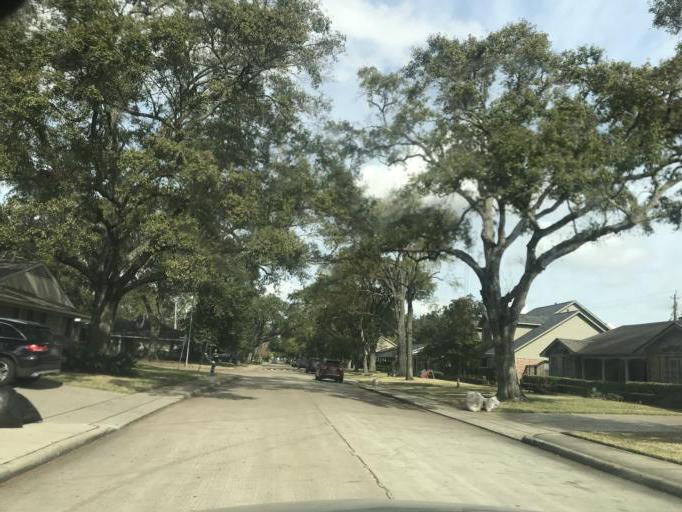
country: US
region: Texas
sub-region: Harris County
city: Hunters Creek Village
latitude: 29.7424
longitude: -95.4898
